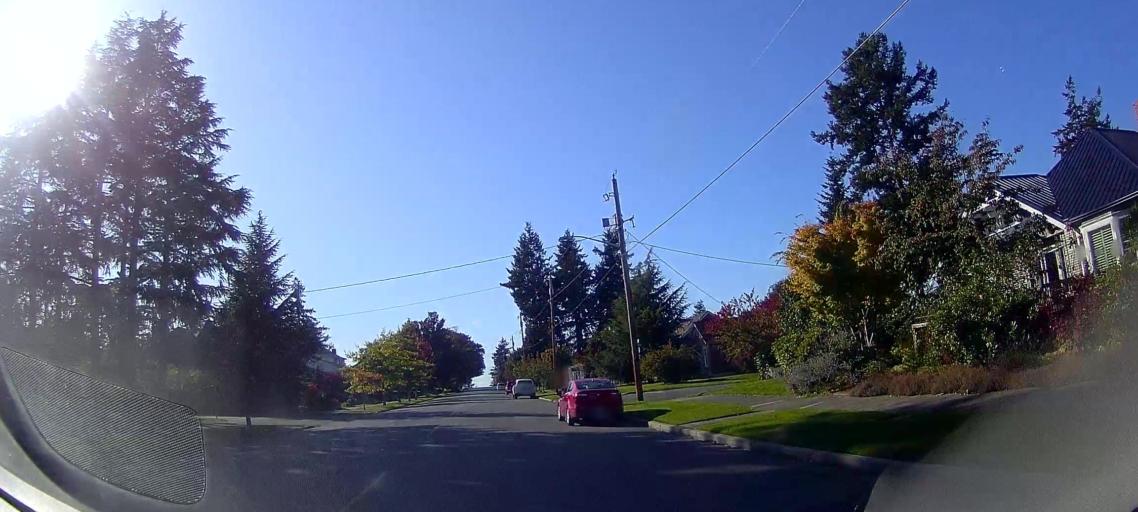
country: US
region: Washington
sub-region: Skagit County
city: Anacortes
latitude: 48.5159
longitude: -122.6216
